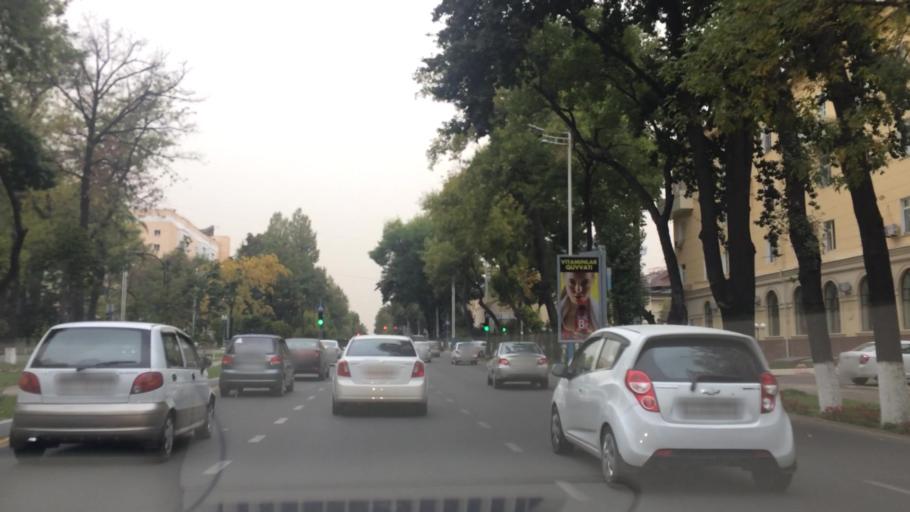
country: UZ
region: Toshkent Shahri
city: Tashkent
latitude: 41.3084
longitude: 69.2901
